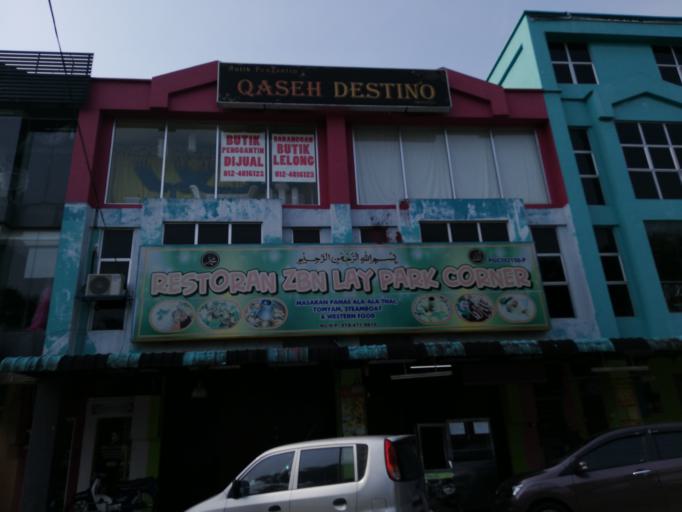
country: MY
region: Kedah
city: Kulim
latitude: 5.3753
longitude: 100.5385
